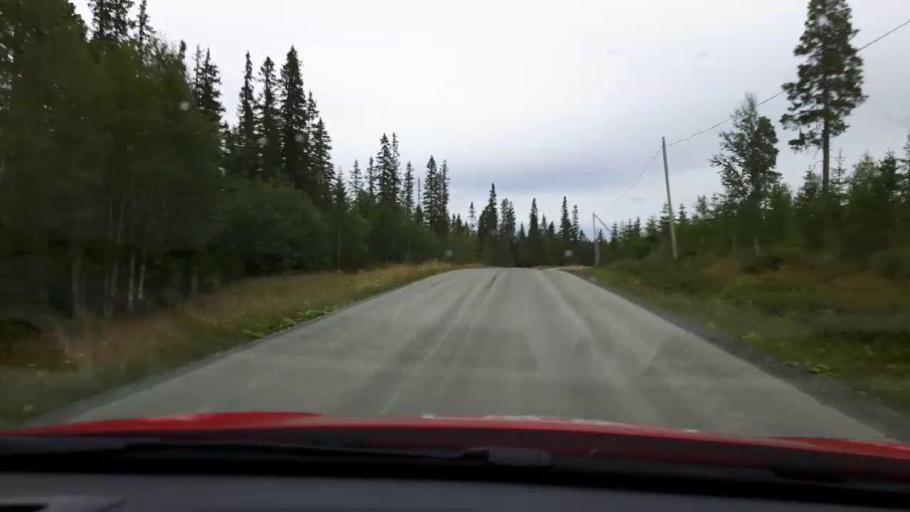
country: SE
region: Jaemtland
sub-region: Are Kommun
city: Jarpen
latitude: 63.4268
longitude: 13.3379
